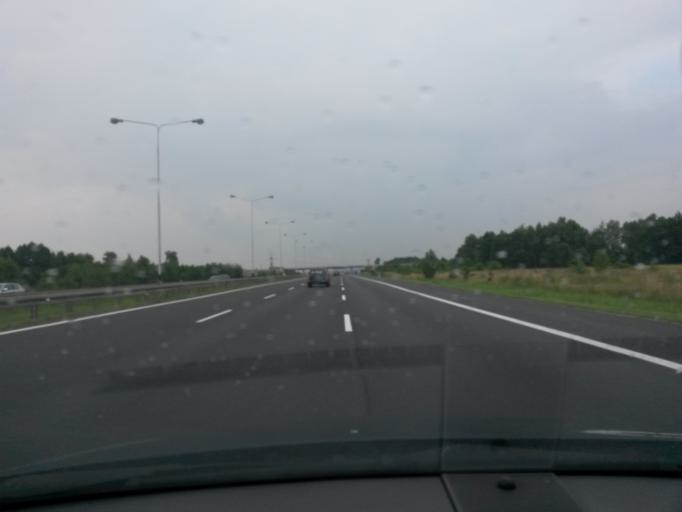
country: PL
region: Lodz Voivodeship
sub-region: Piotrkow Trybunalski
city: Piotrkow Trybunalski
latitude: 51.4225
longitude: 19.6388
